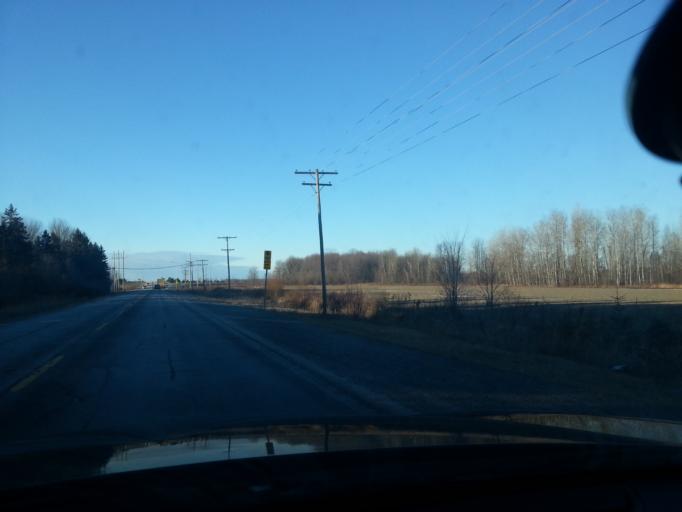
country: CA
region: Ontario
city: Bells Corners
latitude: 45.2127
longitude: -75.7298
